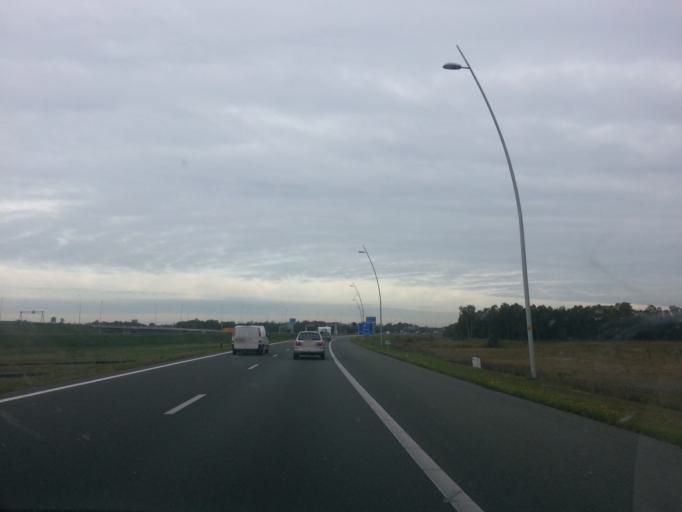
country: NL
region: North Brabant
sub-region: Gemeente Best
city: Best
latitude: 51.4835
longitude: 5.4060
